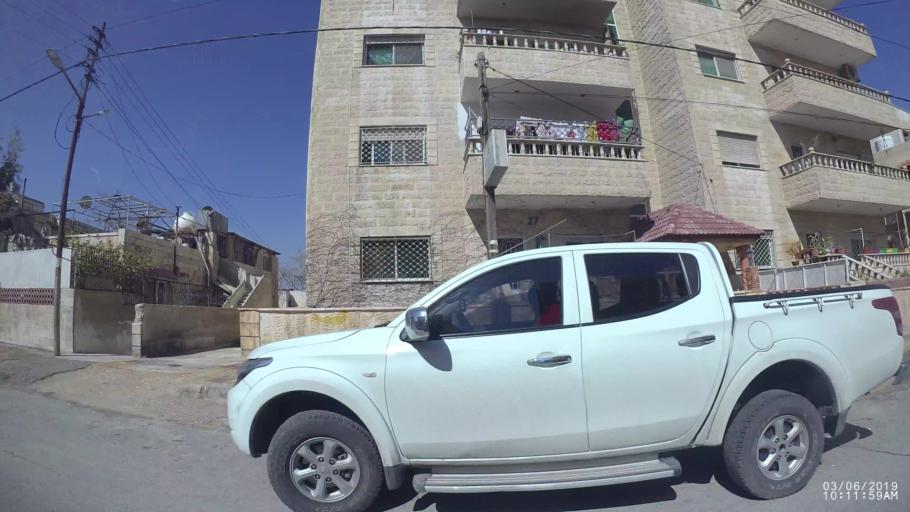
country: JO
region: Amman
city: Amman
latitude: 31.9826
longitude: 35.9857
